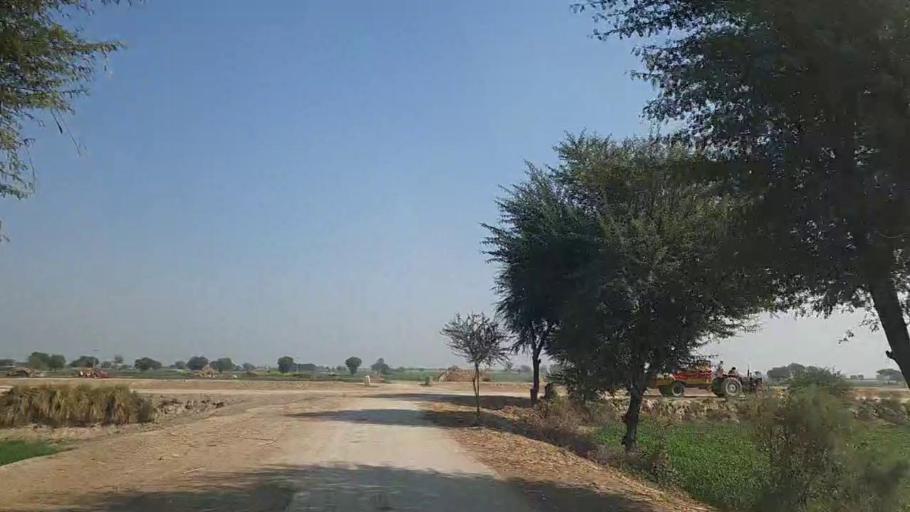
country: PK
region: Sindh
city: Shahpur Chakar
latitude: 26.2026
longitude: 68.5832
